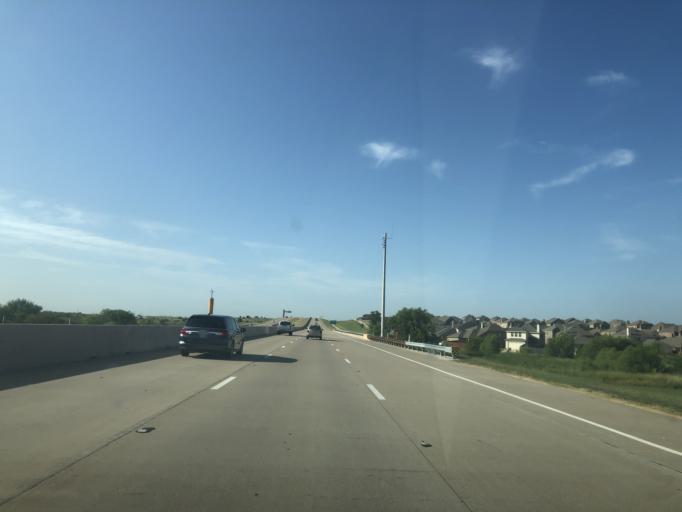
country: US
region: Texas
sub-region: Tarrant County
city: Crowley
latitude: 32.6235
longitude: -97.4127
